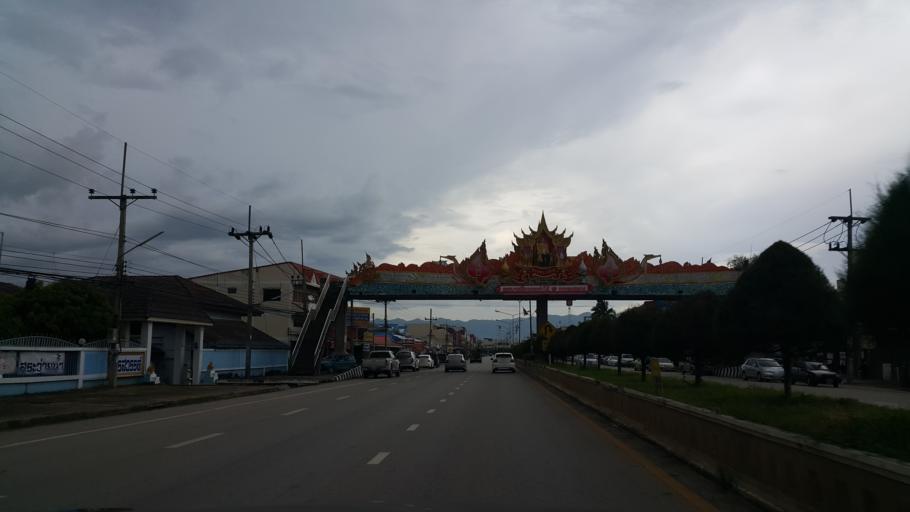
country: TH
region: Phayao
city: Dok Kham Tai
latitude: 19.1620
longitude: 99.9841
